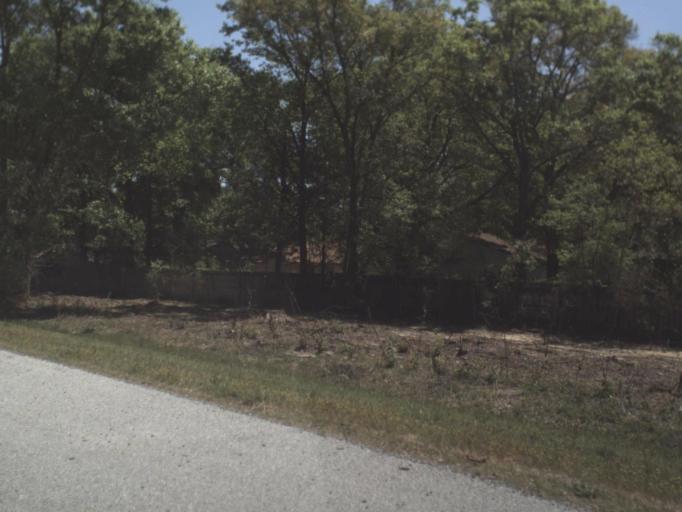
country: US
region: Florida
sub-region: Escambia County
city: Ferry Pass
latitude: 30.5022
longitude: -87.1701
